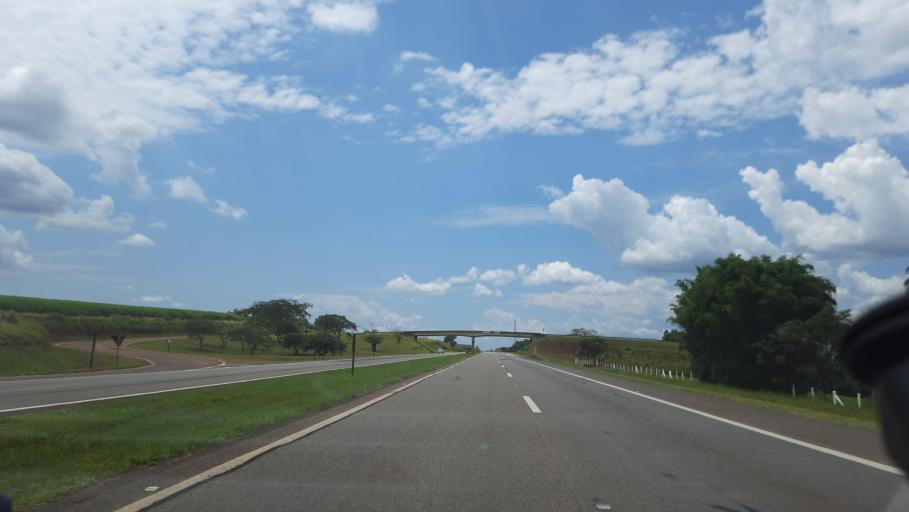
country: BR
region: Sao Paulo
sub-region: Casa Branca
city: Casa Branca
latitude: -21.6977
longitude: -47.0807
